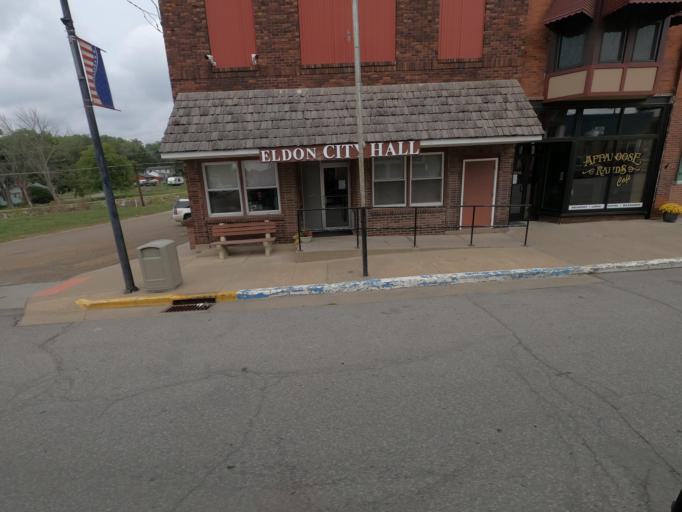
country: US
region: Iowa
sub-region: Wapello County
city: Ottumwa
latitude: 40.9184
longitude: -92.2228
